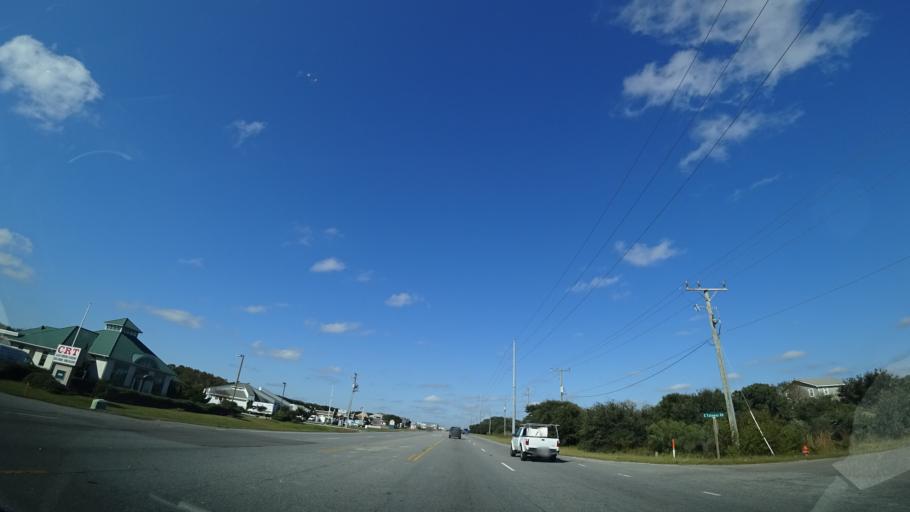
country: US
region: North Carolina
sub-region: Dare County
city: Kitty Hawk
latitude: 36.0568
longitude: -75.6872
